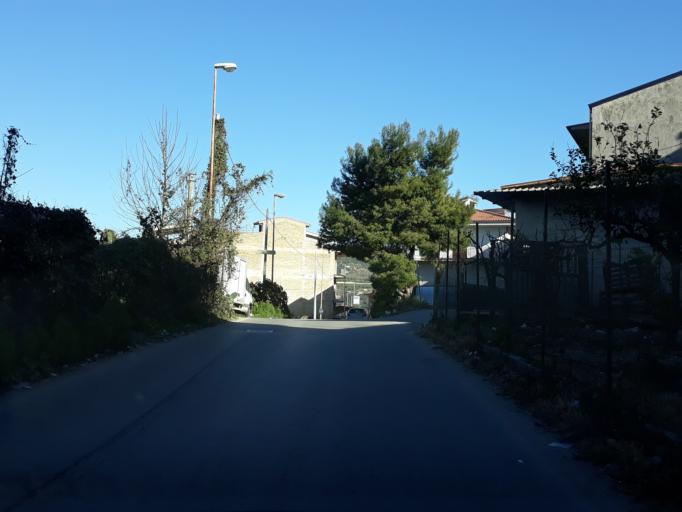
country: IT
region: Sicily
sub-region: Palermo
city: Misilmeri
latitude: 38.0282
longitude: 13.4506
